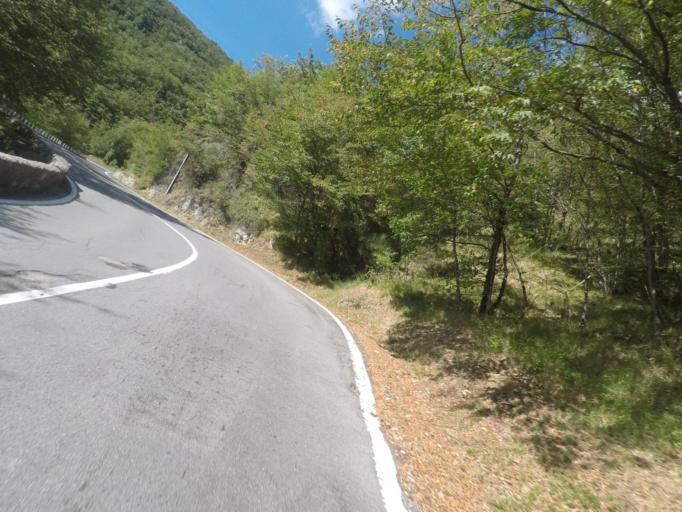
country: IT
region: Tuscany
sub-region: Provincia di Massa-Carrara
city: Fivizzano
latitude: 44.2612
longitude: 10.1751
